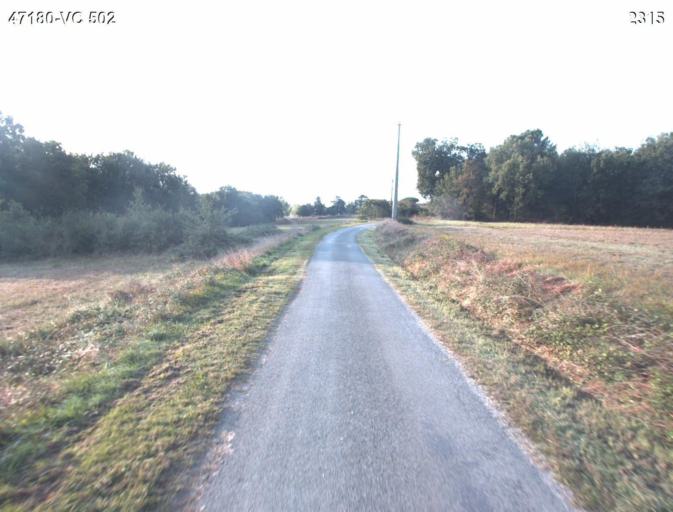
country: FR
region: Aquitaine
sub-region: Departement du Lot-et-Garonne
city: Sainte-Colombe-en-Bruilhois
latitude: 44.1774
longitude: 0.4831
